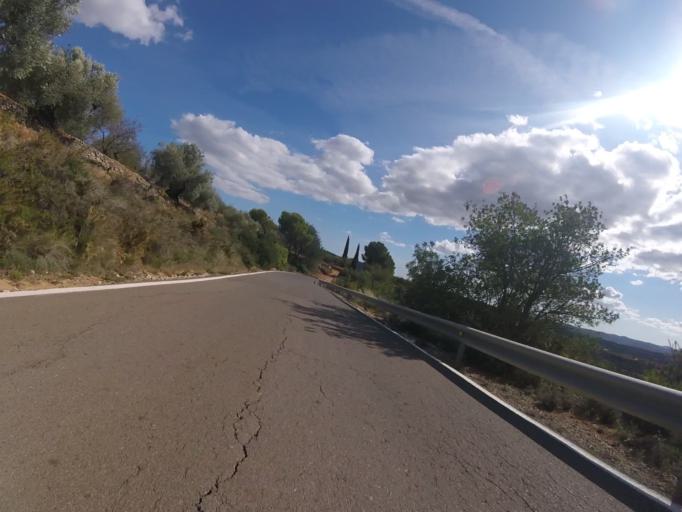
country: ES
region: Valencia
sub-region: Provincia de Castello
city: Cuevas de Vinroma
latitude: 40.3769
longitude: 0.1126
